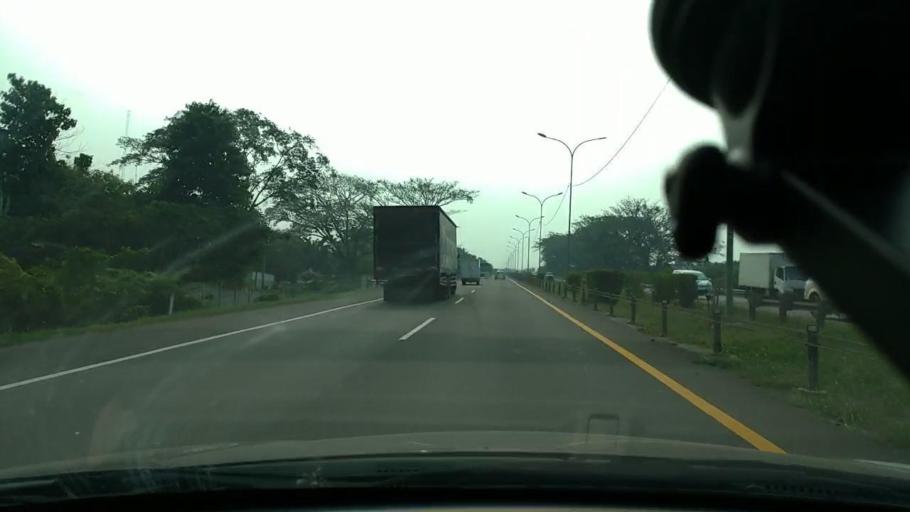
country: ID
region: Banten
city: Serang
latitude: -6.1063
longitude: 106.1773
